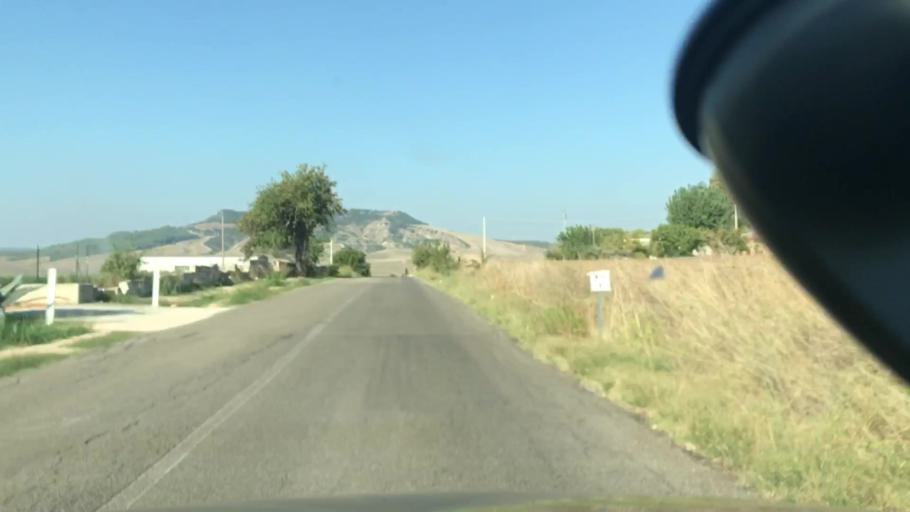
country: IT
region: Basilicate
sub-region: Provincia di Matera
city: La Martella
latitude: 40.6585
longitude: 16.5354
